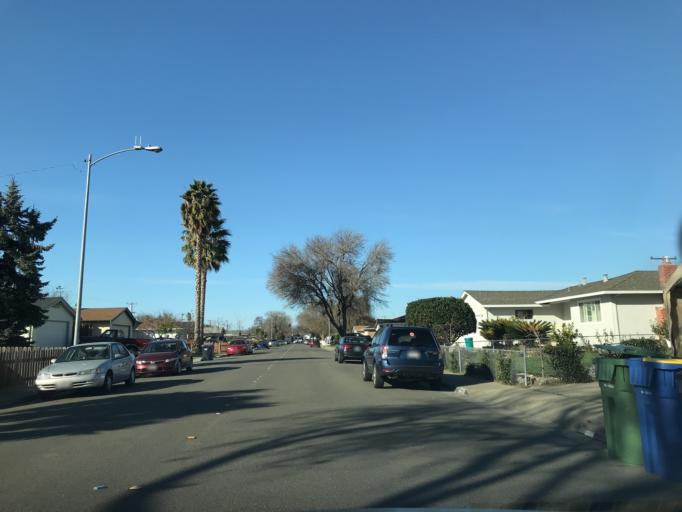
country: US
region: California
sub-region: Santa Clara County
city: Milpitas
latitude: 37.4323
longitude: -121.9168
